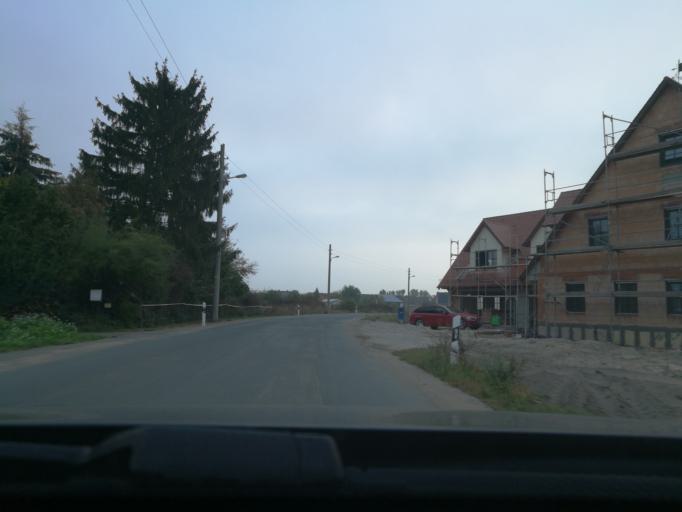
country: DE
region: Bavaria
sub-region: Regierungsbezirk Mittelfranken
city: Wetzendorf
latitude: 49.4935
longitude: 11.0410
